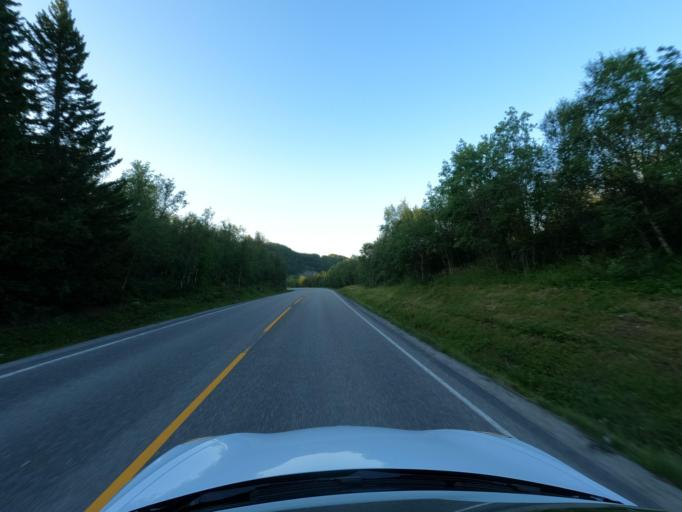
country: NO
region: Troms
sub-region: Harstad
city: Harstad
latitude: 68.7259
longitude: 16.5389
